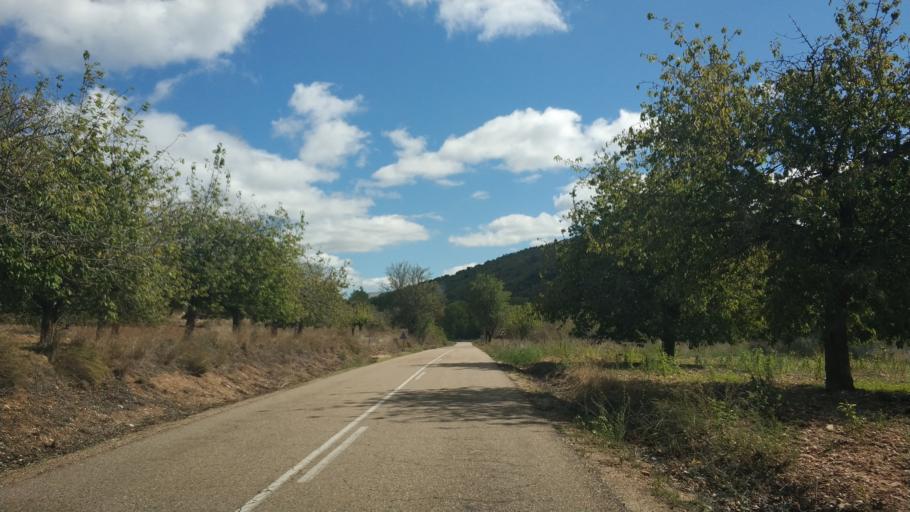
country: ES
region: Castille and Leon
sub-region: Provincia de Burgos
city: Covarrubias
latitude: 42.0560
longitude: -3.5112
